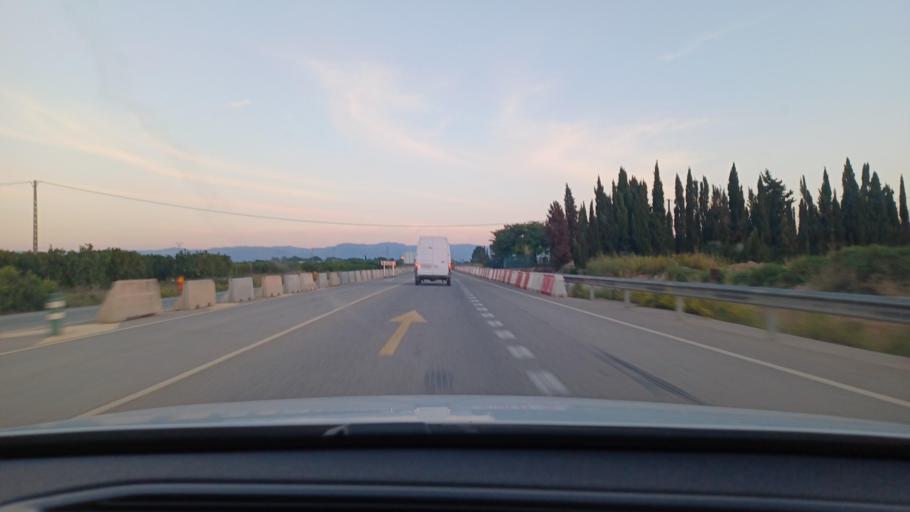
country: ES
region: Catalonia
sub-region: Provincia de Tarragona
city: Alcanar
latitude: 40.5480
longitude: 0.4349
